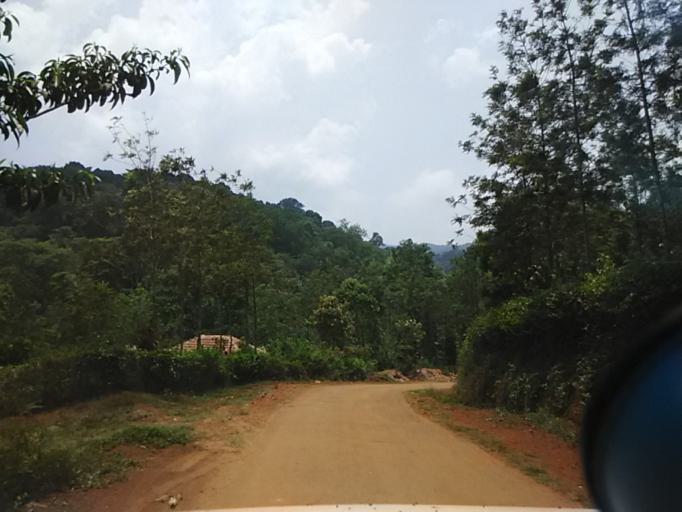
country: IN
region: Karnataka
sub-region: Kodagu
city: Virarajendrapet
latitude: 12.2114
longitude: 75.6765
